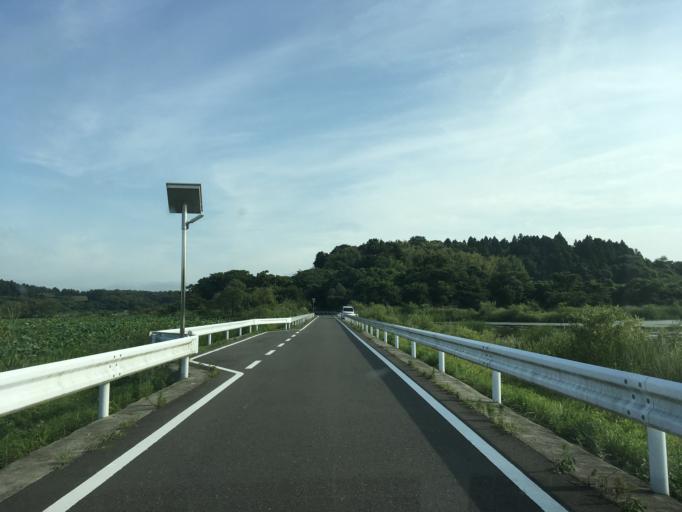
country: JP
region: Miyagi
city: Wakuya
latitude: 38.6892
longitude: 141.1066
